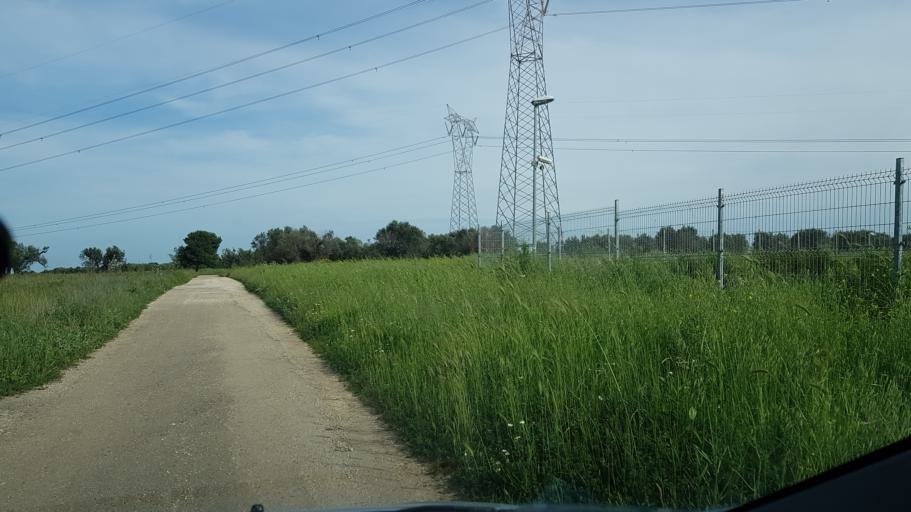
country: IT
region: Apulia
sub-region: Provincia di Brindisi
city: Tuturano
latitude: 40.5537
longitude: 17.9296
